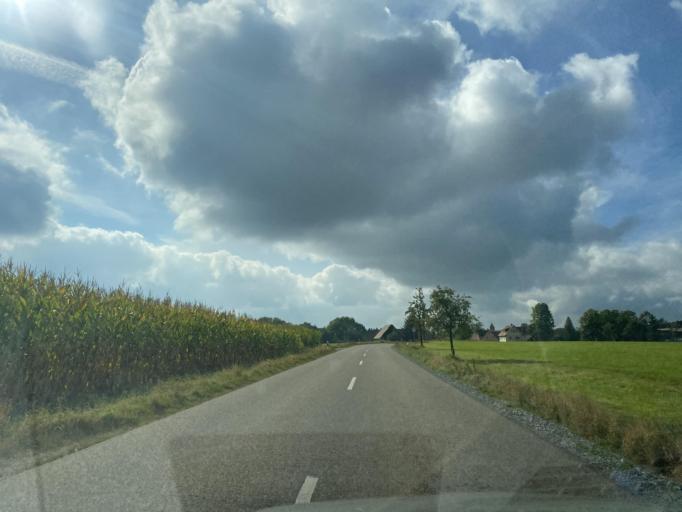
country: DE
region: Baden-Wuerttemberg
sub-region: Regierungsbezirk Stuttgart
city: Buhlertann
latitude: 49.0437
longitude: 9.9586
